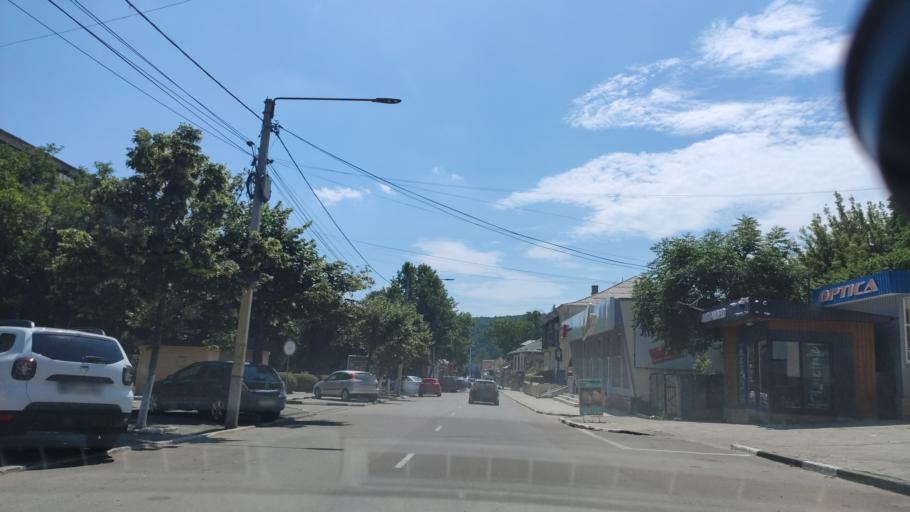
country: MD
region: Raionul Soroca
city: Soroca
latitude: 48.1601
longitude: 28.3006
